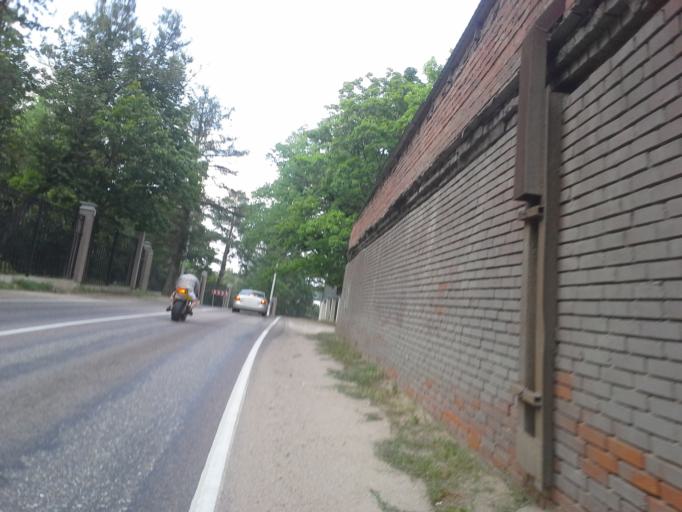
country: RU
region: Moskovskaya
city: Istra
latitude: 55.8956
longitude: 36.7938
